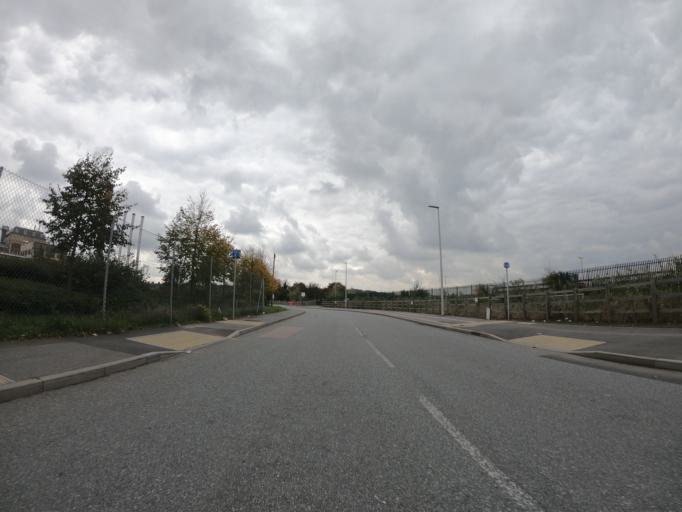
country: GB
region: England
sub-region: Greater London
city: Erith
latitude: 51.4951
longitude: 0.1683
